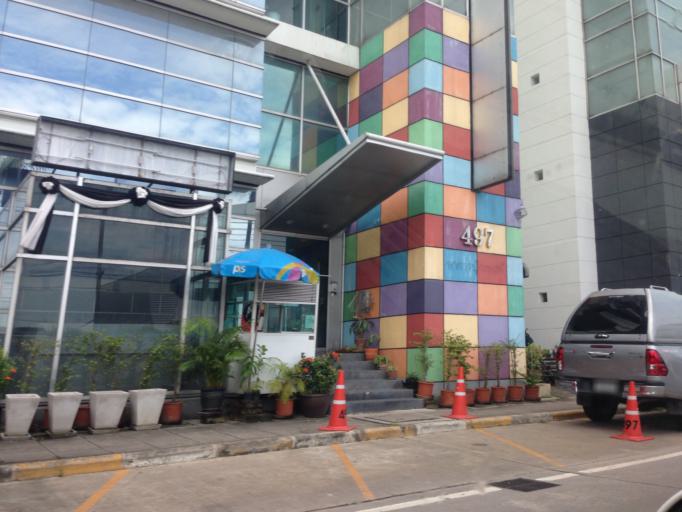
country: TH
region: Nonthaburi
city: Pak Kret
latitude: 13.9286
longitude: 100.5320
